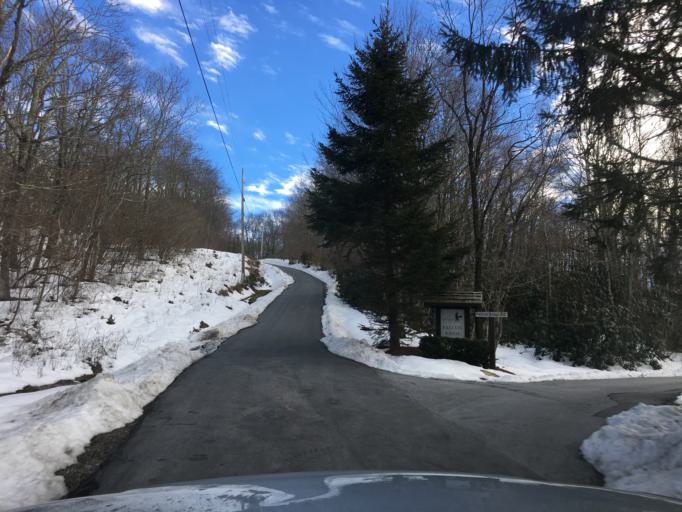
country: US
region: North Carolina
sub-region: Jackson County
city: Cullowhee
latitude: 35.1351
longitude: -82.9909
